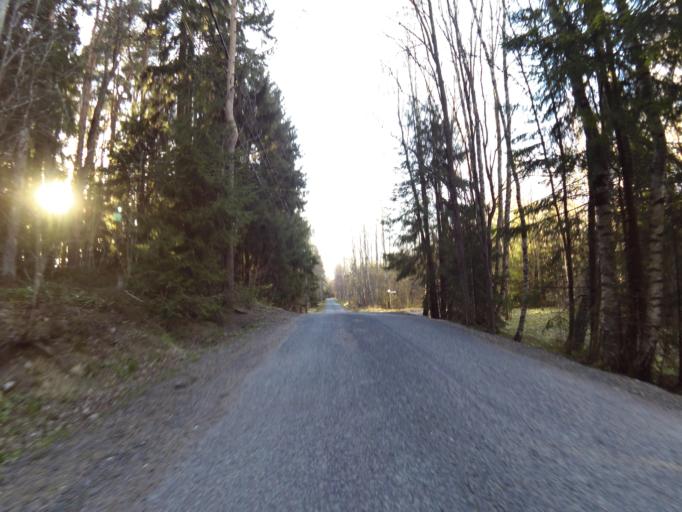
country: FI
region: Uusimaa
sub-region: Helsinki
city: Espoo
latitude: 60.1797
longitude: 24.6892
